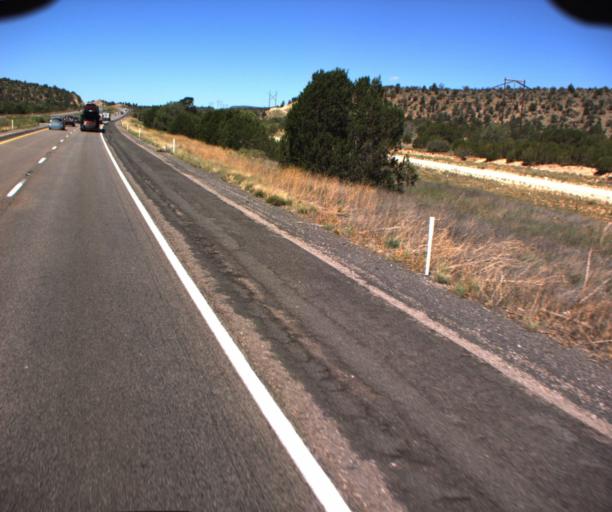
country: US
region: Arizona
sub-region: Mohave County
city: Peach Springs
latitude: 35.3028
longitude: -113.0051
